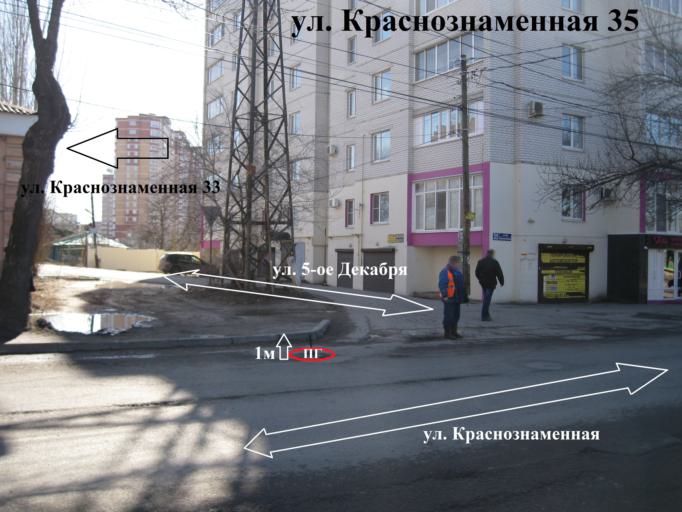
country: RU
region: Voronezj
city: Voronezh
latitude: 51.6504
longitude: 39.1862
